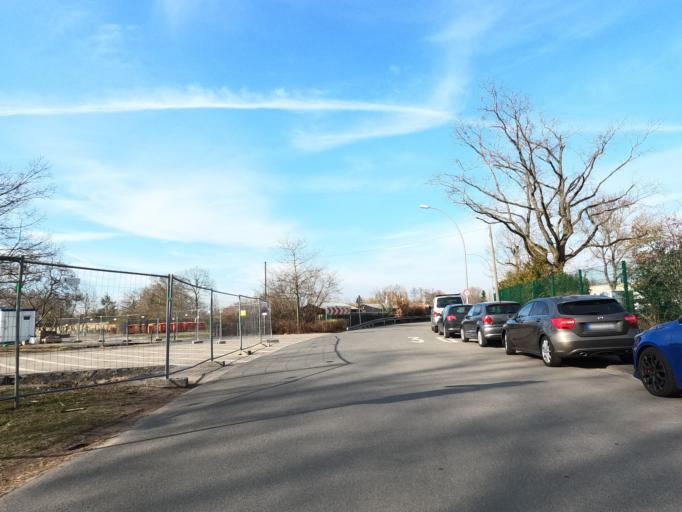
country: DE
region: Hesse
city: Raunheim
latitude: 50.0026
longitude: 8.4568
